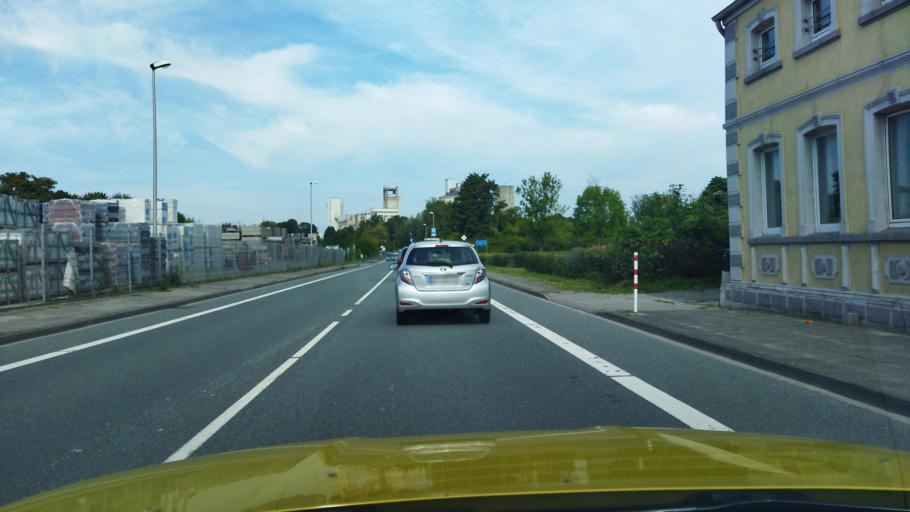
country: DE
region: North Rhine-Westphalia
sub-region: Regierungsbezirk Munster
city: Ennigerloh
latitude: 51.8187
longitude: 8.0249
